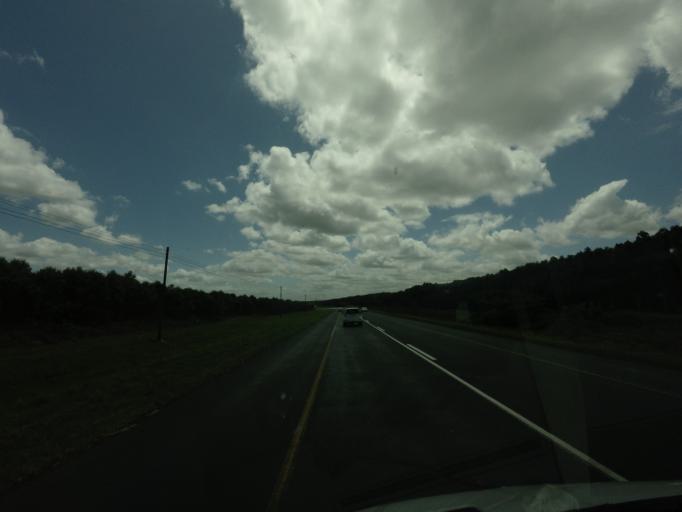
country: ZA
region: KwaZulu-Natal
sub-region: uThungulu District Municipality
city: KwaMbonambi
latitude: -28.5694
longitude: 32.1113
